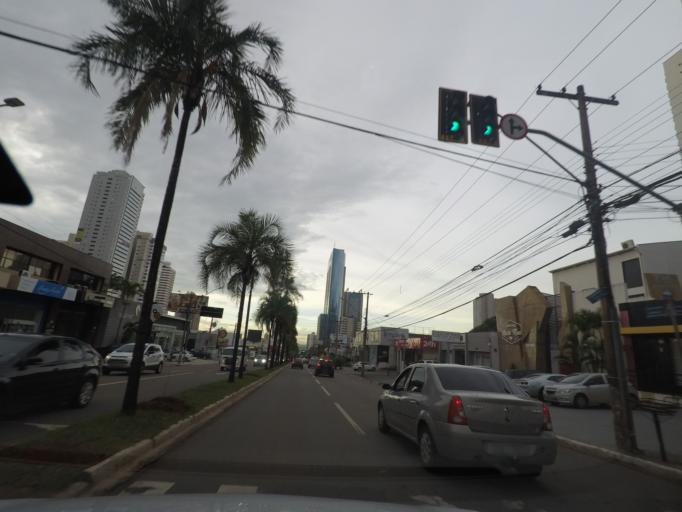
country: BR
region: Goias
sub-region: Goiania
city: Goiania
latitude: -16.7005
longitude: -49.2673
